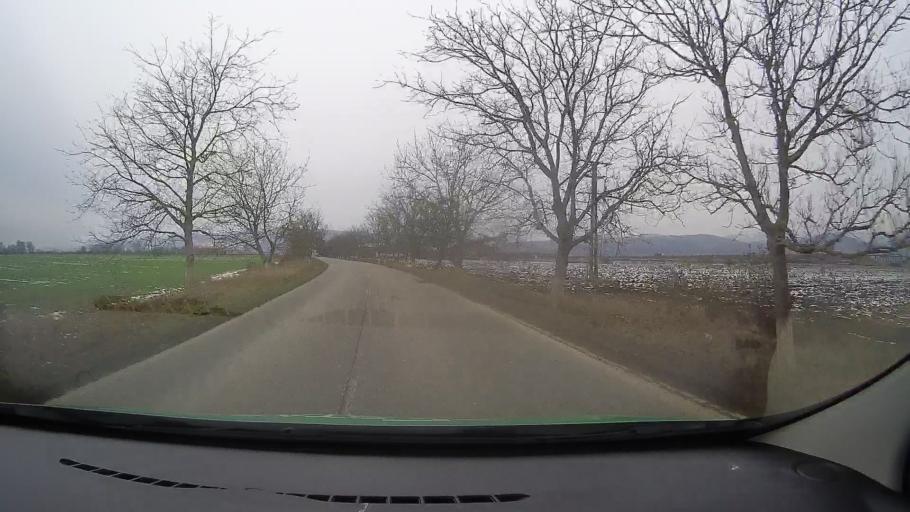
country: RO
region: Hunedoara
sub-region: Comuna Romos
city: Romos
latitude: 45.8819
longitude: 23.2548
